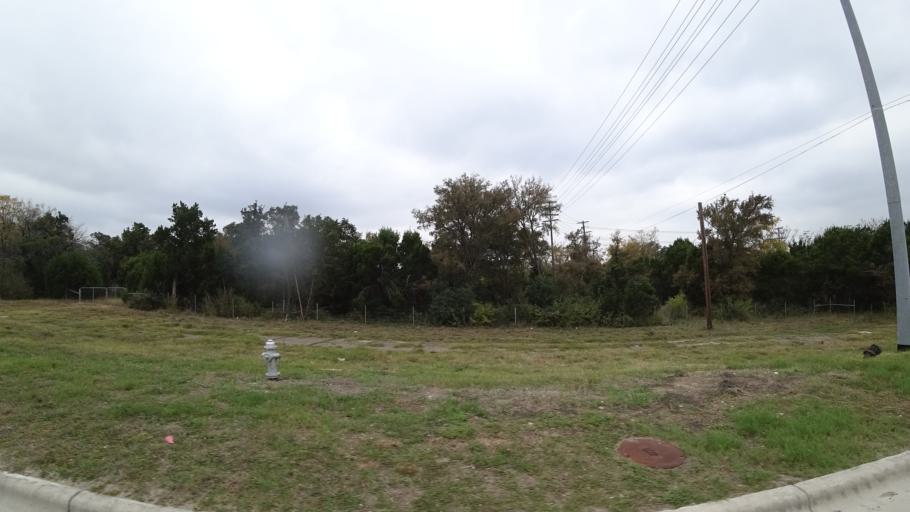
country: US
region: Texas
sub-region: Williamson County
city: Anderson Mill
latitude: 30.4561
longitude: -97.8293
